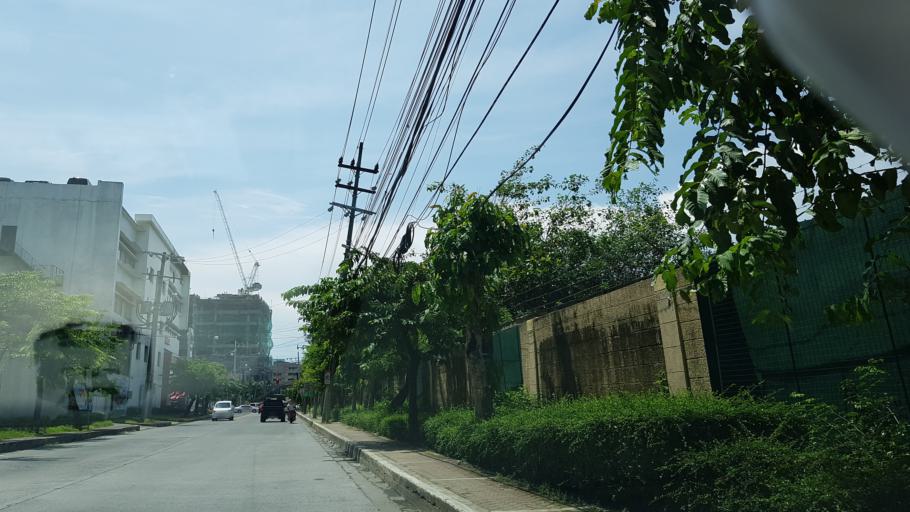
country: PH
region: Metro Manila
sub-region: Makati City
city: Makati City
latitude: 14.5638
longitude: 121.0177
